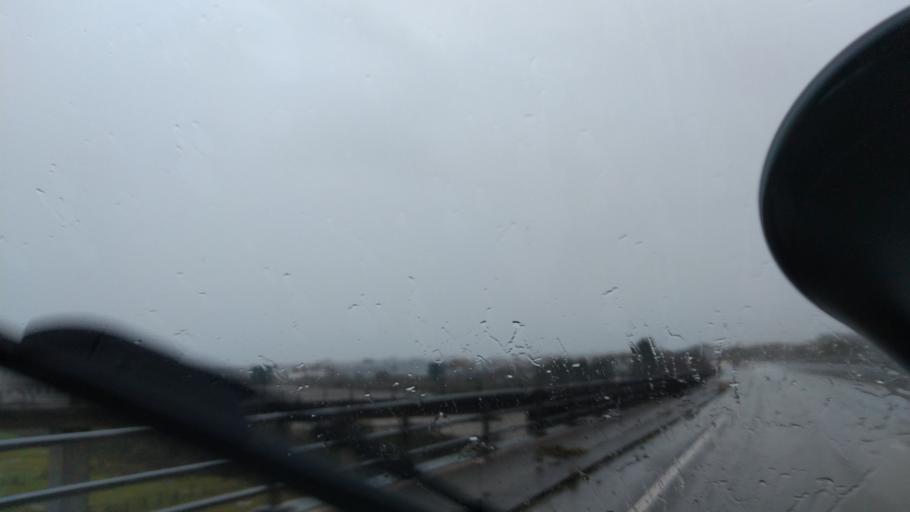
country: GB
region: England
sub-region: West Sussex
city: Shoreham-by-Sea
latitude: 50.8447
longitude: -0.2860
